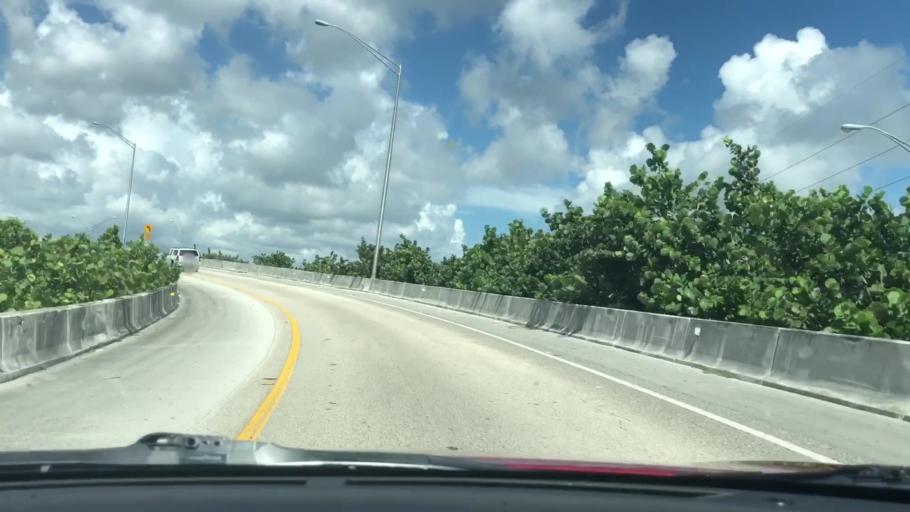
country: US
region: Florida
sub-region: Palm Beach County
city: West Palm Beach
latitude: 26.7076
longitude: -80.0754
